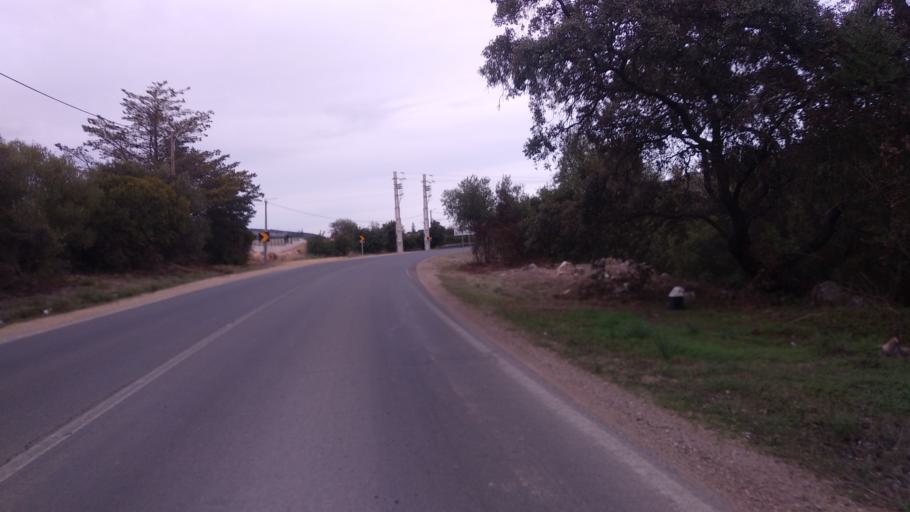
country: PT
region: Faro
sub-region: Faro
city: Santa Barbara de Nexe
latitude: 37.1492
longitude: -7.9538
